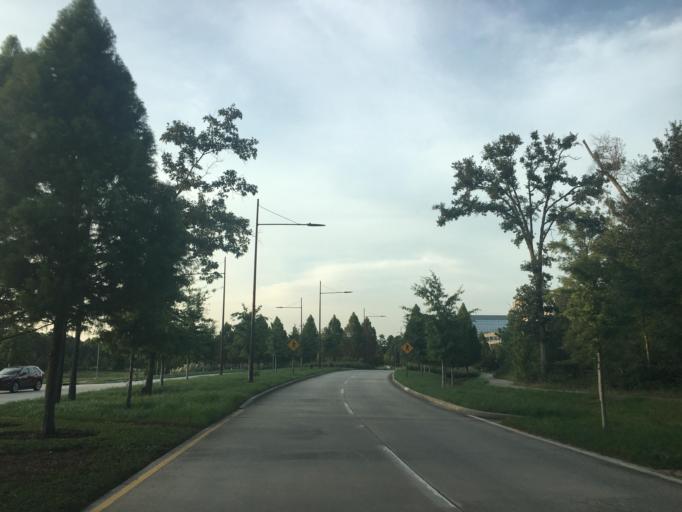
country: US
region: Texas
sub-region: Harris County
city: Spring
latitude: 30.1009
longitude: -95.4387
